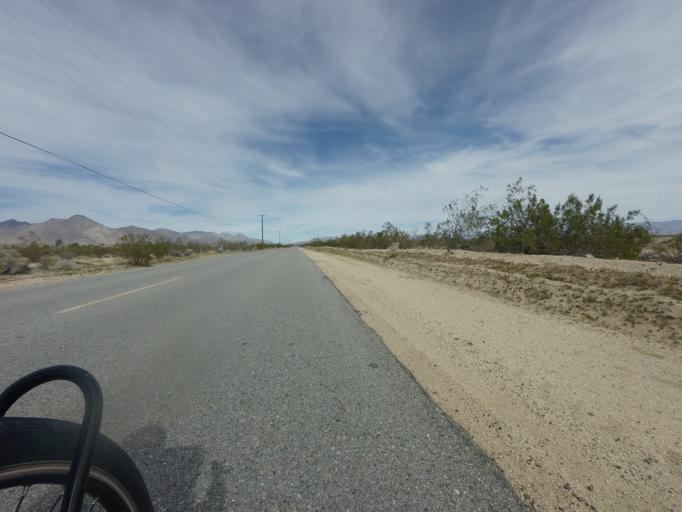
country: US
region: California
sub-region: Kern County
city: Inyokern
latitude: 35.7336
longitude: -117.8380
